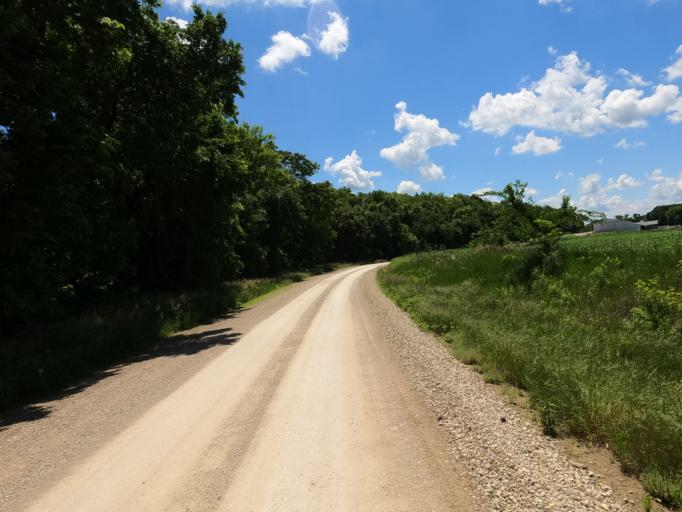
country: US
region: Kansas
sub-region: Marion County
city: Marion
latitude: 38.2443
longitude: -96.8074
